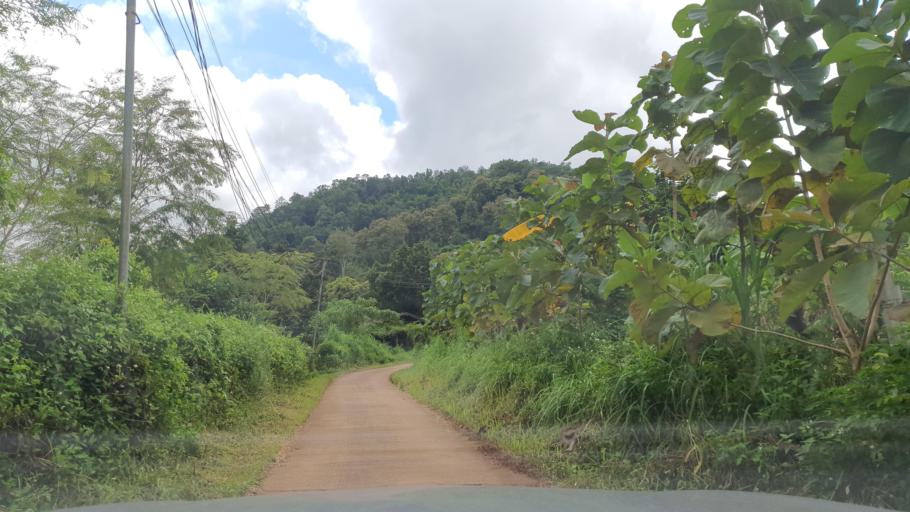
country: TH
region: Chiang Mai
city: Samoeng
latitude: 18.8076
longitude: 98.8196
